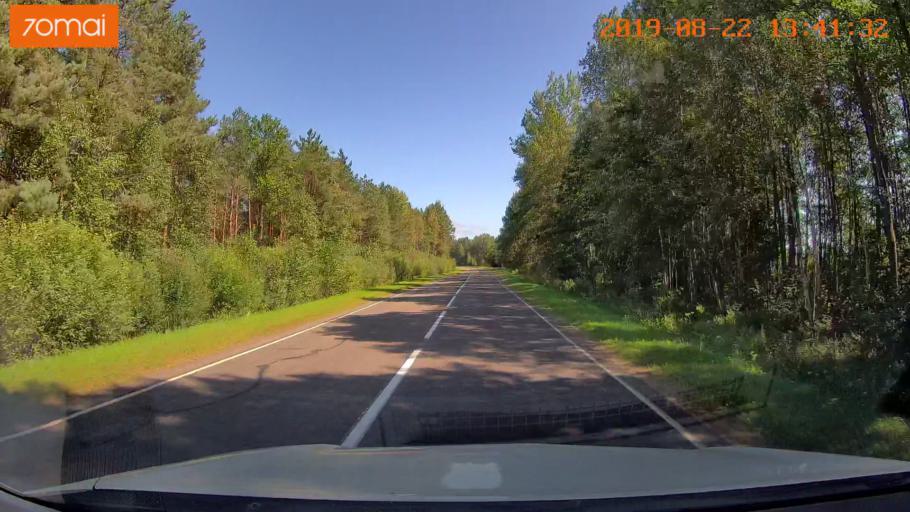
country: BY
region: Minsk
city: Staryya Darohi
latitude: 53.2387
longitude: 28.4001
